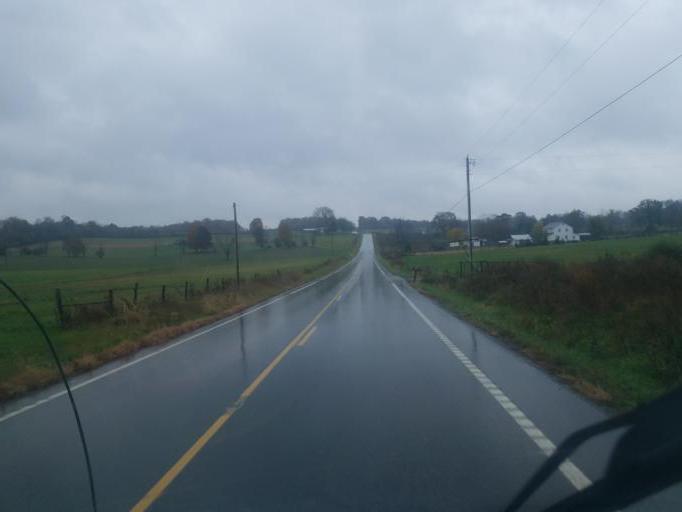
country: US
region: Ohio
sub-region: Licking County
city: Utica
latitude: 40.2381
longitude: -82.3030
